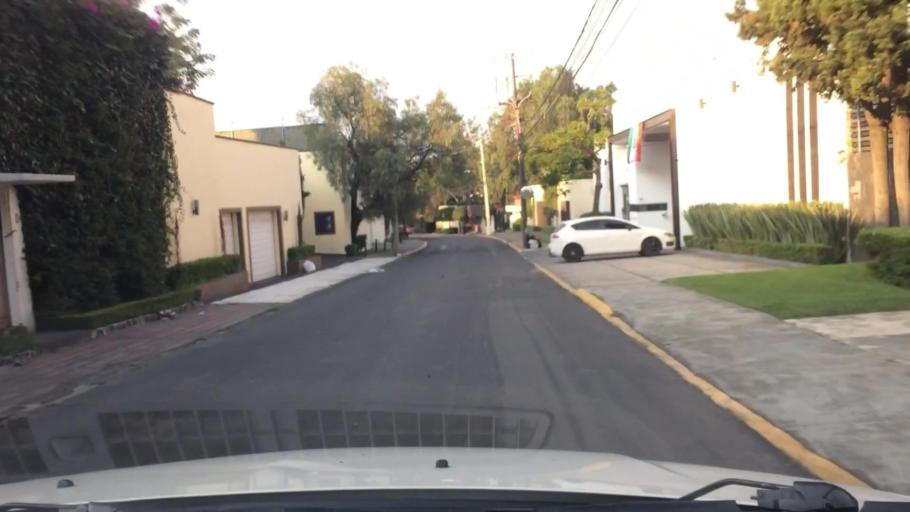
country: MX
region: Mexico City
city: Magdalena Contreras
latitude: 19.3221
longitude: -99.2086
